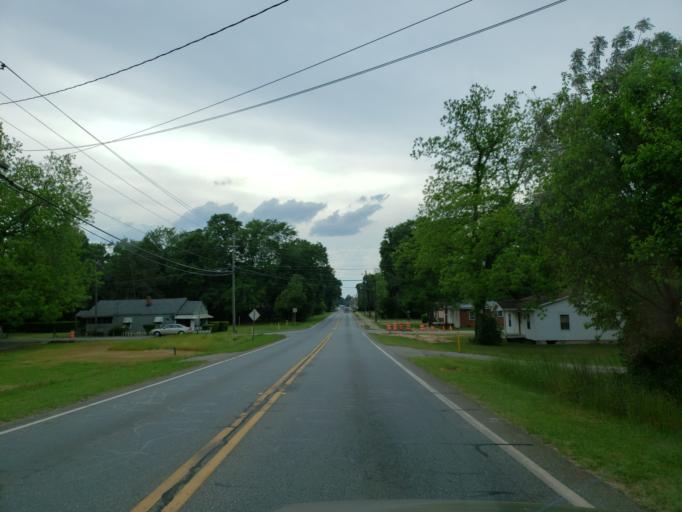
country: US
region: Georgia
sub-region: Macon County
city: Montezuma
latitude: 32.2935
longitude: -84.0117
